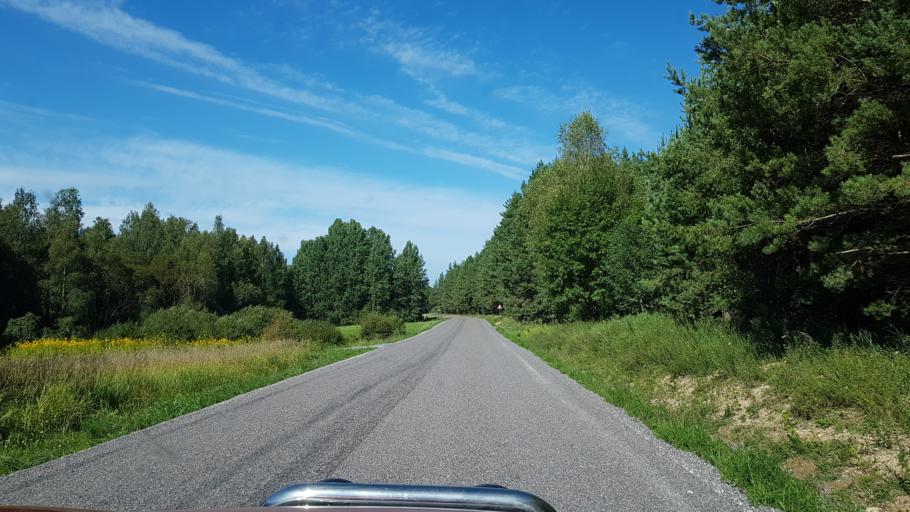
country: EE
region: Tartu
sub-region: Elva linn
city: Elva
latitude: 58.2479
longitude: 26.3783
